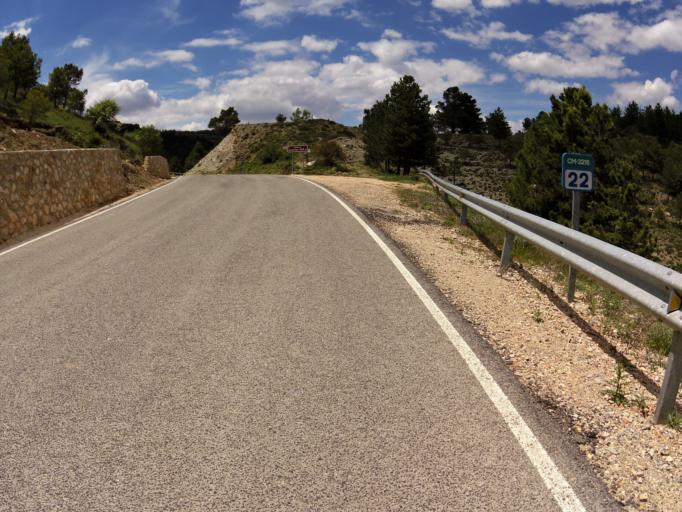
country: ES
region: Castille-La Mancha
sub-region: Provincia de Albacete
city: Paterna del Madera
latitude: 38.5762
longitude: -2.4176
